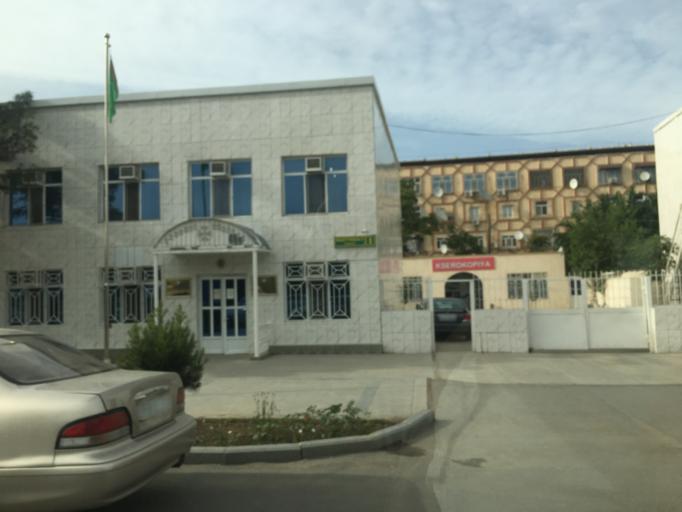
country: TM
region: Mary
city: Mary
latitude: 37.5893
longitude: 61.8376
